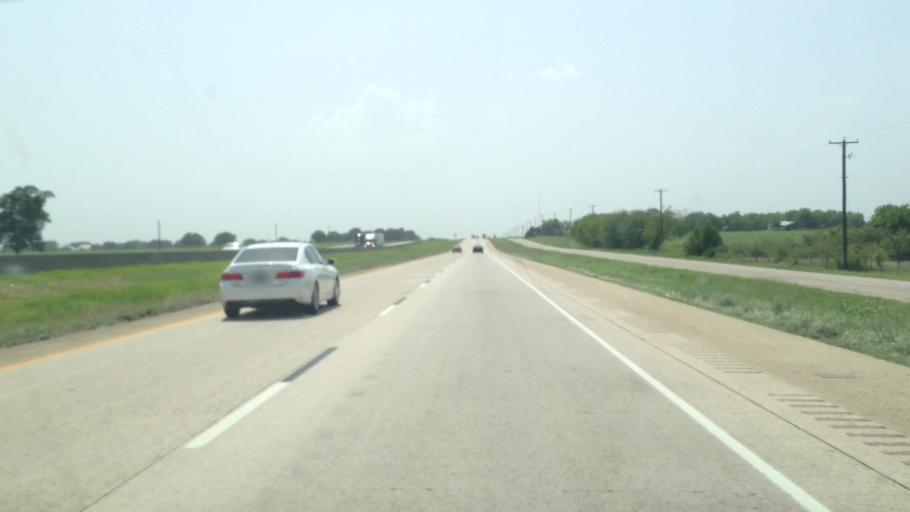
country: US
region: Texas
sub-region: Hopkins County
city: Sulphur Springs
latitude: 33.1209
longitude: -95.6941
